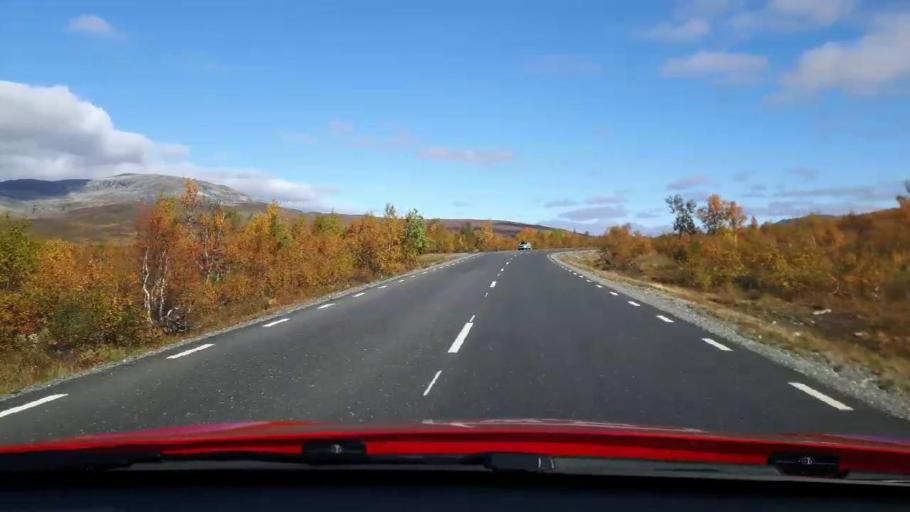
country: NO
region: Nordland
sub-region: Hattfjelldal
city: Hattfjelldal
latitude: 64.9990
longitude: 14.2416
